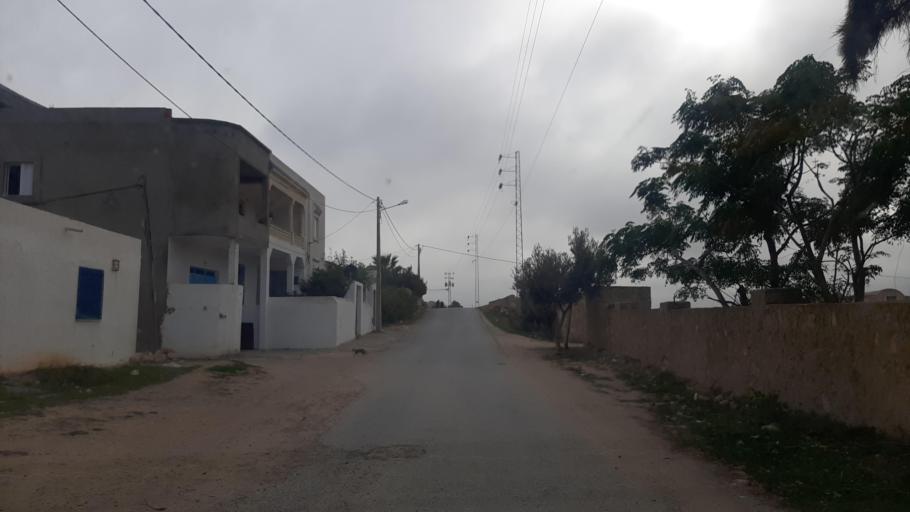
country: TN
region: Nabul
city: Menzel Heurr
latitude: 36.6781
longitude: 10.9237
